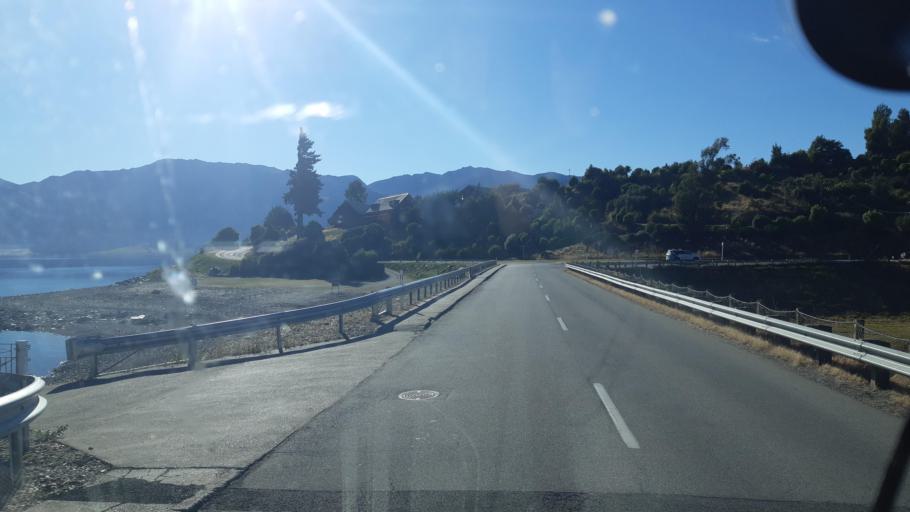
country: NZ
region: Otago
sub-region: Queenstown-Lakes District
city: Wanaka
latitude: -44.6102
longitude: 169.2505
